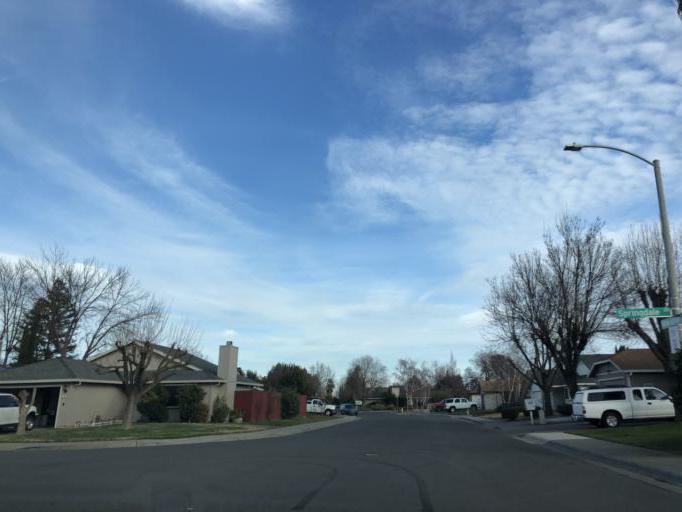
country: US
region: California
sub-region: Yolo County
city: Woodland
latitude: 38.6703
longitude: -121.7555
